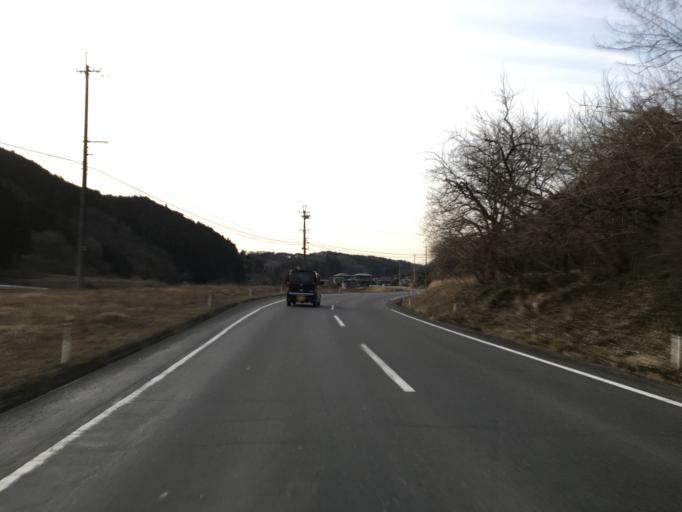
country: JP
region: Fukushima
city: Ishikawa
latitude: 37.0334
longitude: 140.3541
